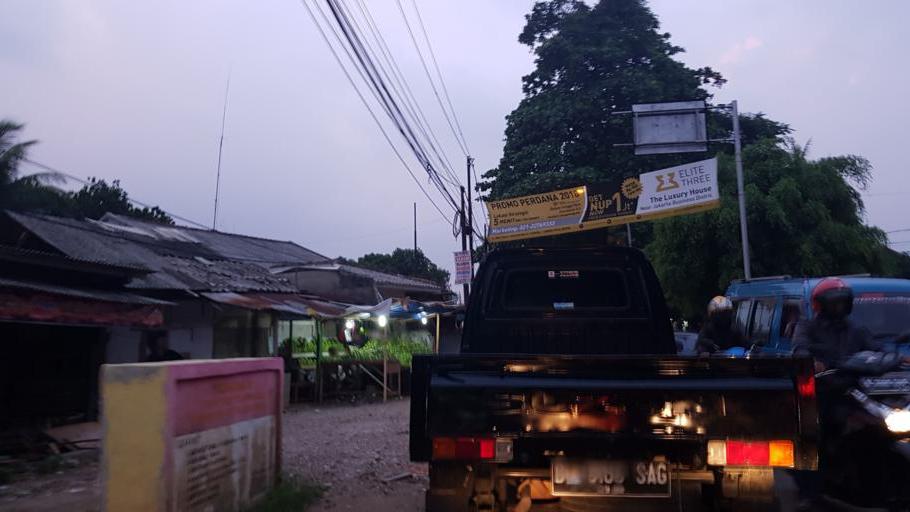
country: ID
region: West Java
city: Depok
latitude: -6.3680
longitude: 106.8079
